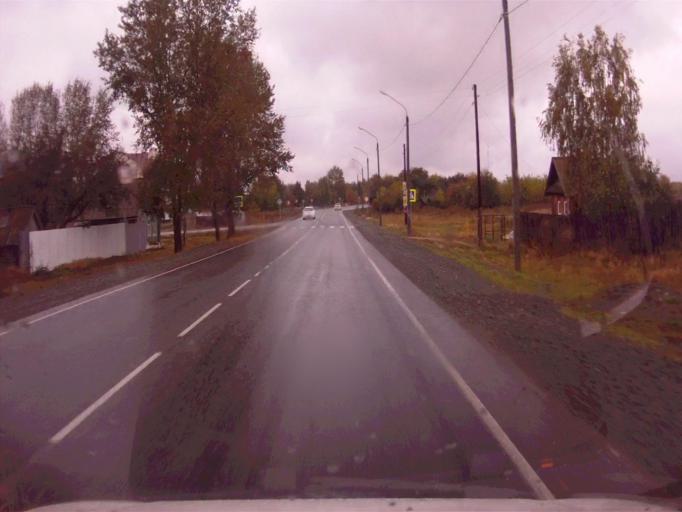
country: RU
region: Chelyabinsk
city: Tayginka
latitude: 55.4969
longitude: 60.6465
